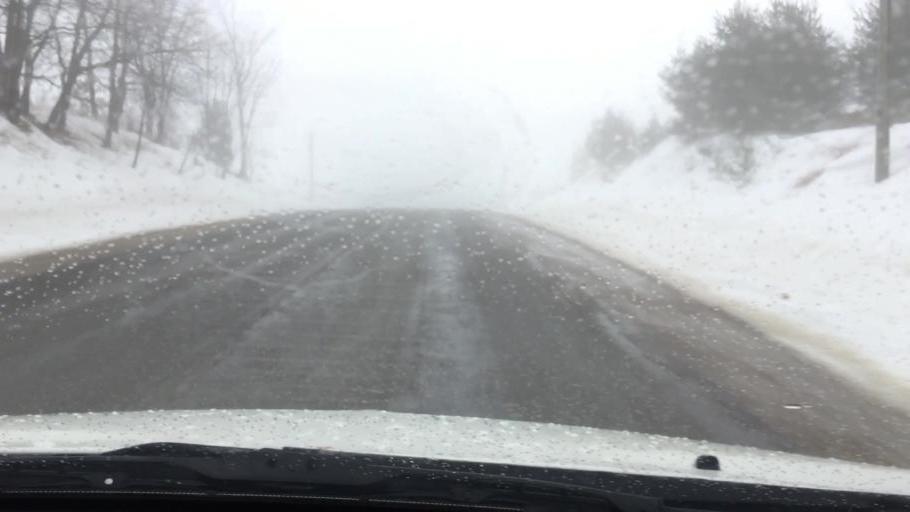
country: US
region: Michigan
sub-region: Charlevoix County
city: East Jordan
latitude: 45.1325
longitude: -85.1752
